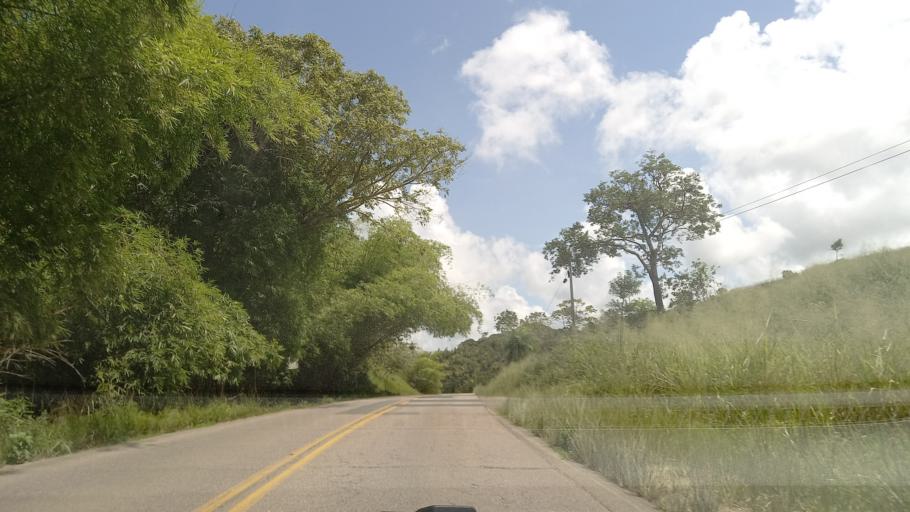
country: BR
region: Pernambuco
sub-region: Barreiros
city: Barreiros
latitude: -8.7665
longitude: -35.1688
